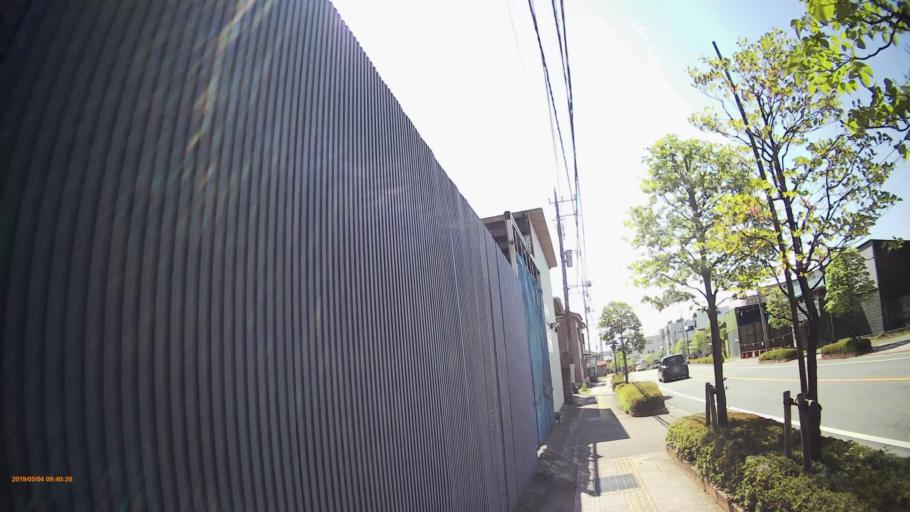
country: JP
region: Yamanashi
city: Nirasaki
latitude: 35.7114
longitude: 138.4450
